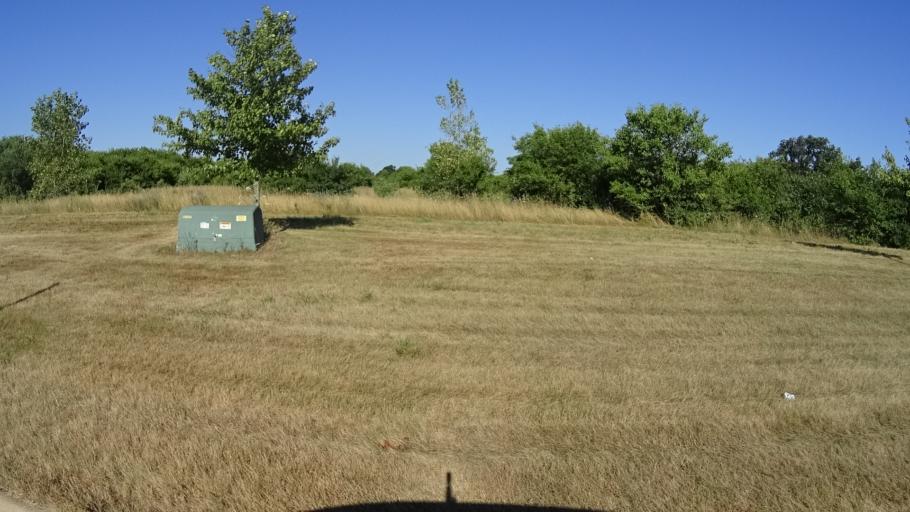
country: US
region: Ohio
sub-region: Erie County
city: Sandusky
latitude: 41.4115
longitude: -82.7613
